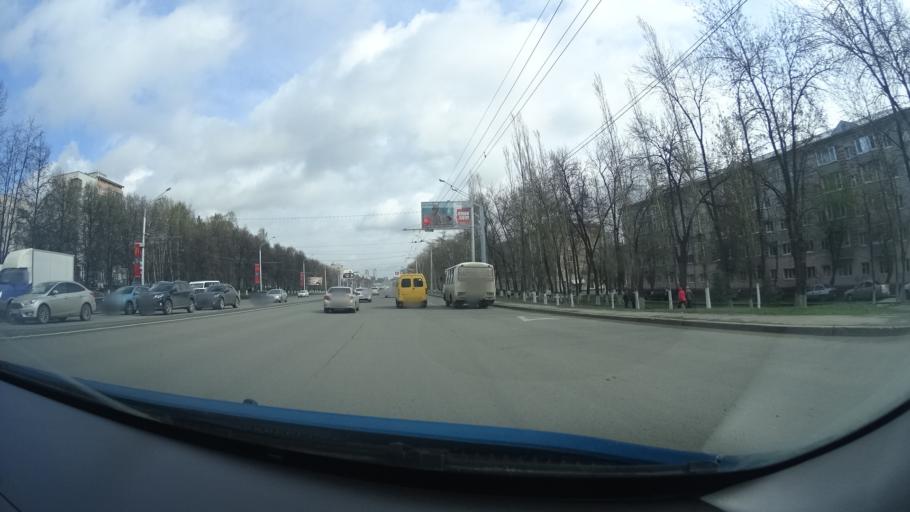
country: RU
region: Bashkortostan
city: Ufa
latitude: 54.7470
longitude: 55.9907
